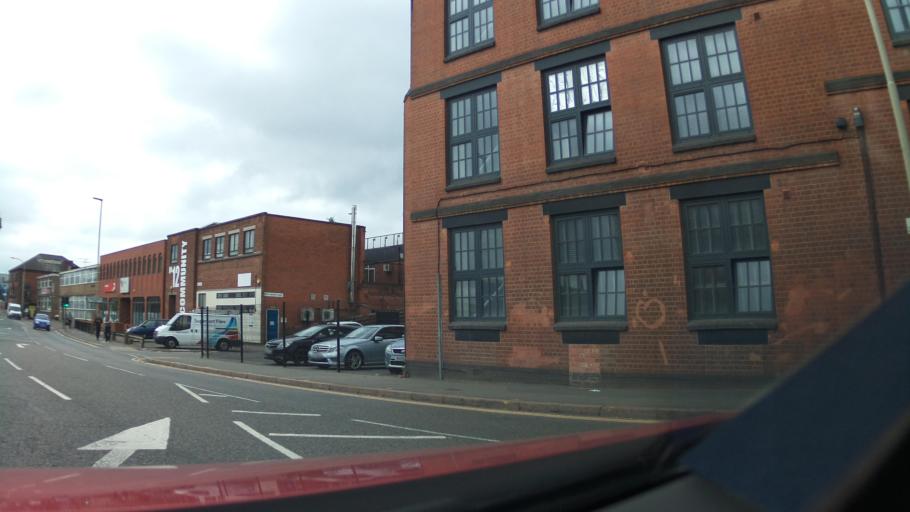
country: GB
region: England
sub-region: City of Leicester
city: Leicester
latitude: 52.6425
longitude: -1.1437
